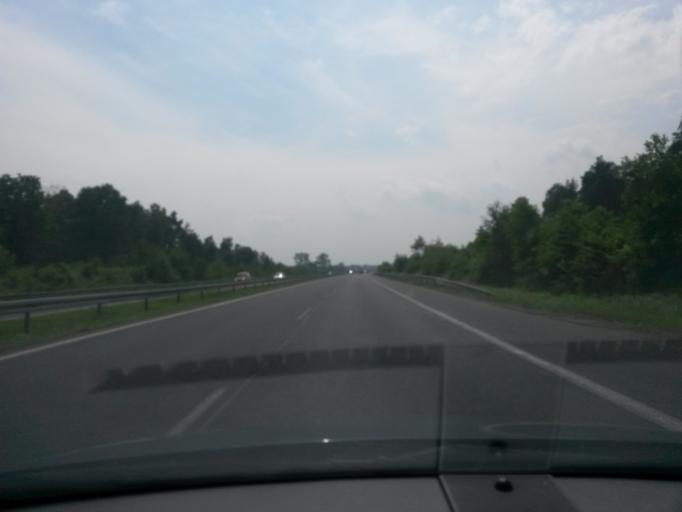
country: PL
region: Lodz Voivodeship
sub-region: Powiat radomszczanski
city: Kamiensk
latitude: 51.2423
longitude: 19.5216
